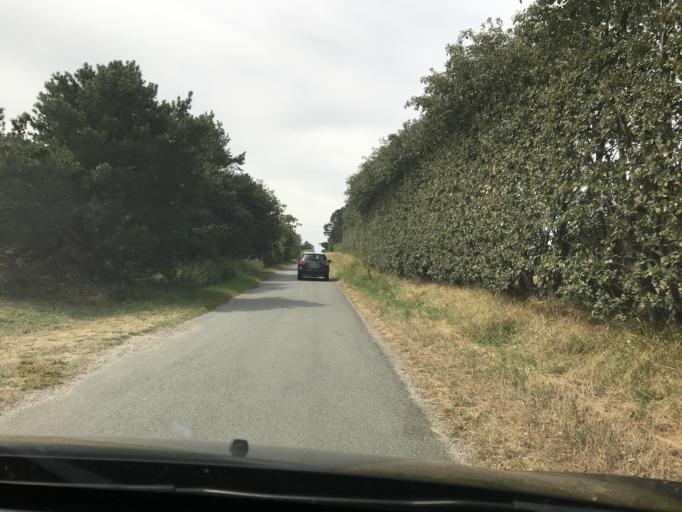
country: DK
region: South Denmark
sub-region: Faaborg-Midtfyn Kommune
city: Faaborg
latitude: 54.9342
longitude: 10.2478
